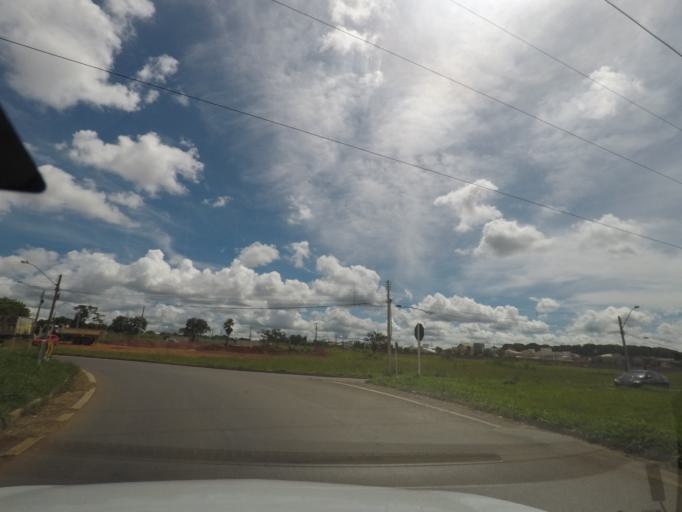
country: BR
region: Goias
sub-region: Goiania
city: Goiania
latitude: -16.7517
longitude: -49.3399
